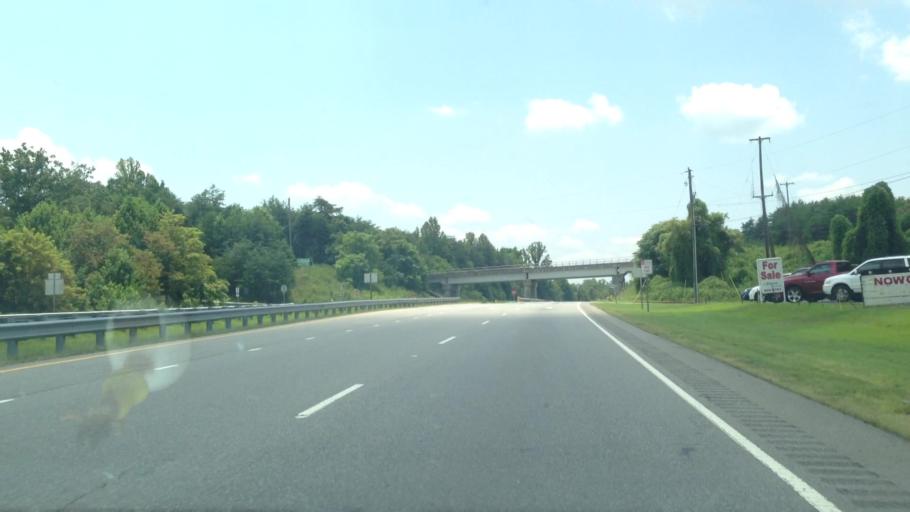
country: US
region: North Carolina
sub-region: Rockingham County
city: Stoneville
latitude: 36.5345
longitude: -79.9137
